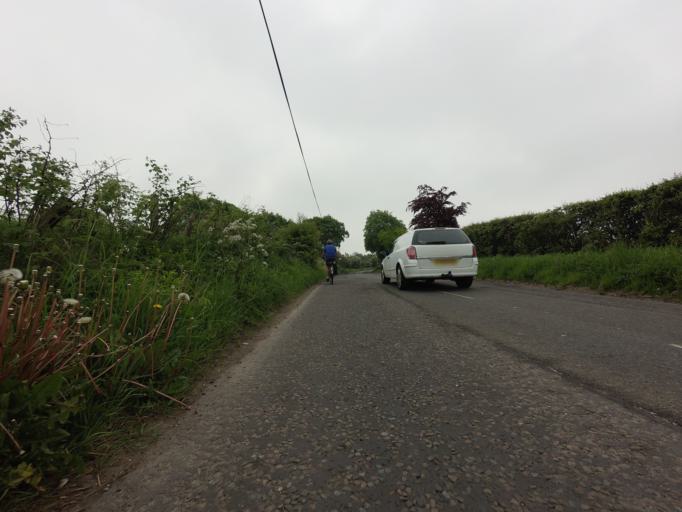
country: GB
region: Scotland
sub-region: Fife
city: Townhill
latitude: 56.1005
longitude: -3.4501
